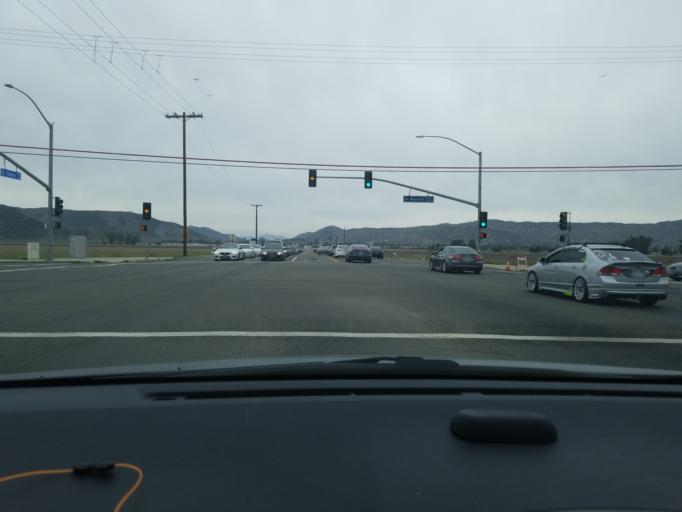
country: US
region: California
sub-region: Riverside County
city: Green Acres
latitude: 33.7439
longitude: -117.0326
